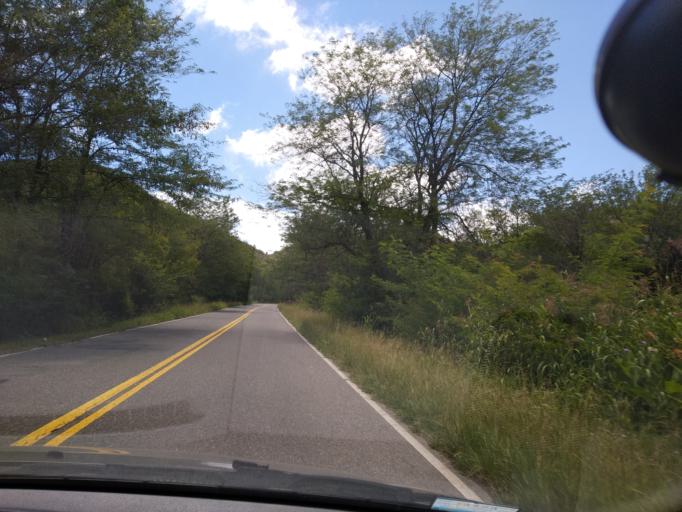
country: AR
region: Cordoba
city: Cuesta Blanca
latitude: -31.6057
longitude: -64.5577
